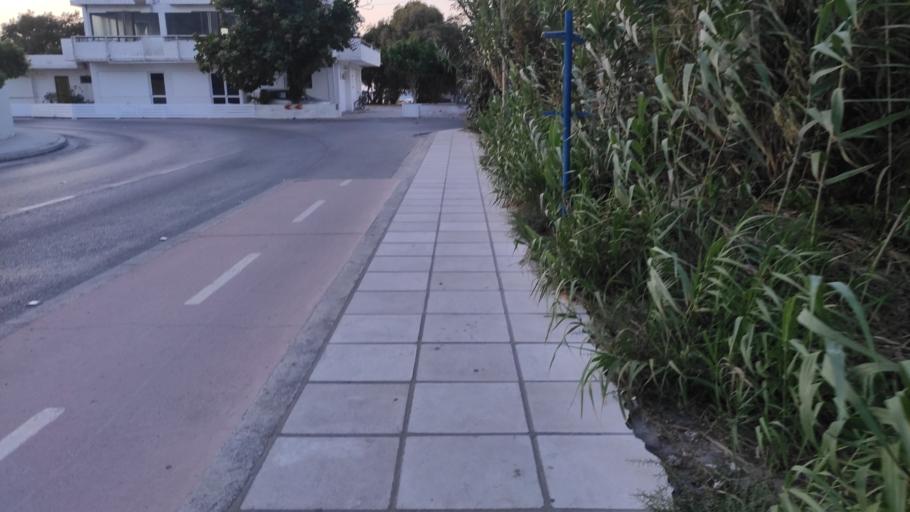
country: GR
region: South Aegean
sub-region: Nomos Dodekanisou
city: Kos
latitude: 36.9143
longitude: 27.2778
